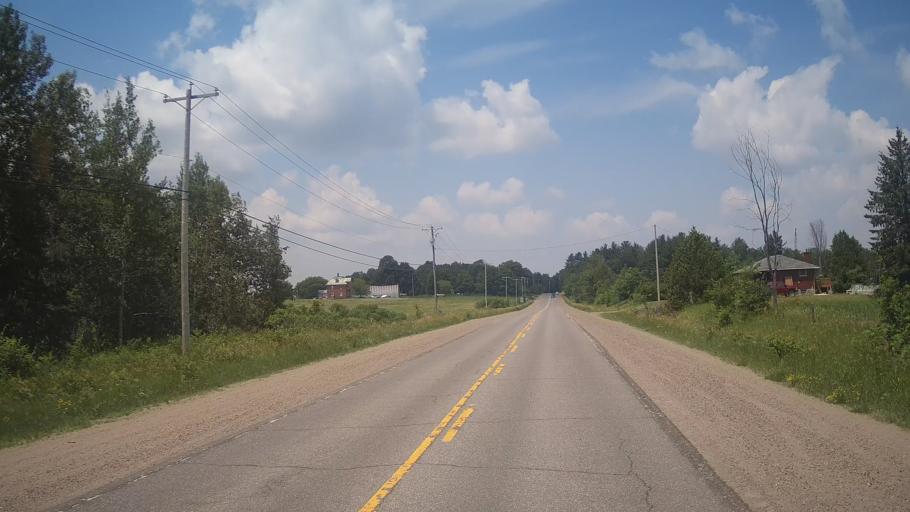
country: CA
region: Quebec
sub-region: Outaouais
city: Shawville
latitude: 45.5721
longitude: -76.4399
